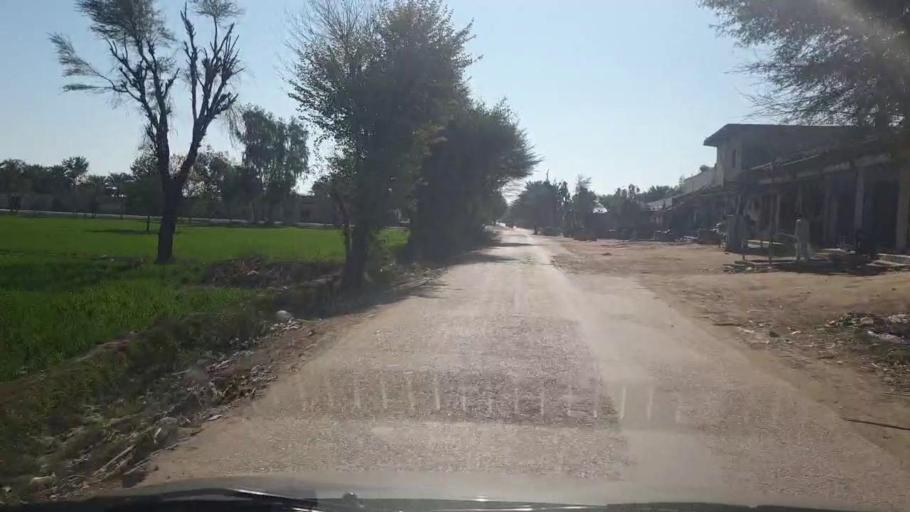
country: PK
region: Sindh
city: Bozdar
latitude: 27.1770
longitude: 68.6400
